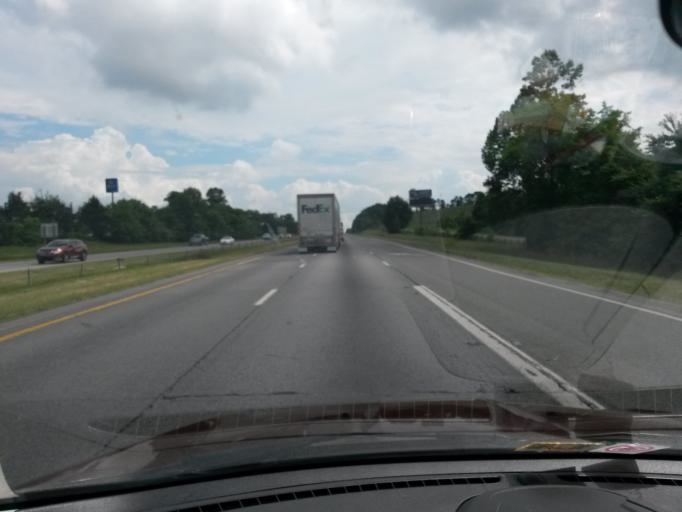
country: US
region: North Carolina
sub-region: Yadkin County
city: Jonesville
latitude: 36.1952
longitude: -80.8117
